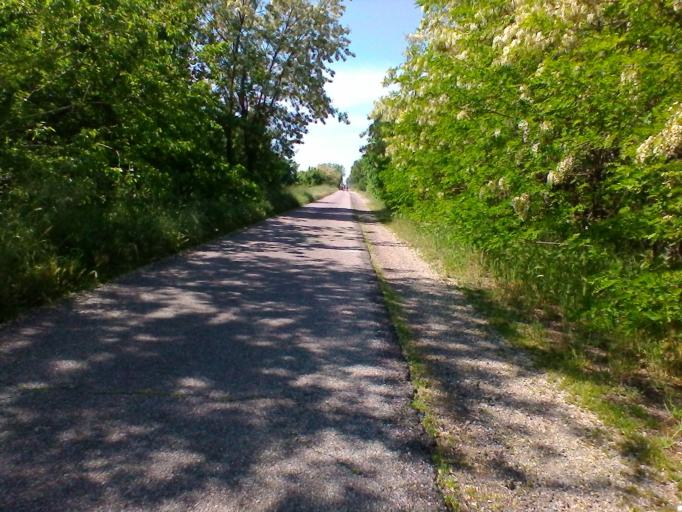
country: IT
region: Lombardy
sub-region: Provincia di Mantova
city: Soave
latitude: 45.2174
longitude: 10.7175
